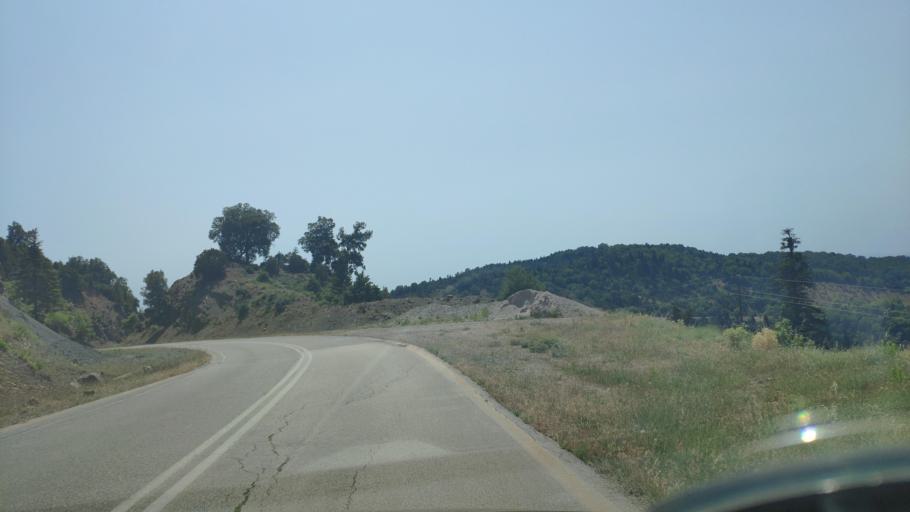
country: GR
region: Epirus
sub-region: Nomos Artas
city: Ano Kalentini
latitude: 39.2374
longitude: 21.2287
